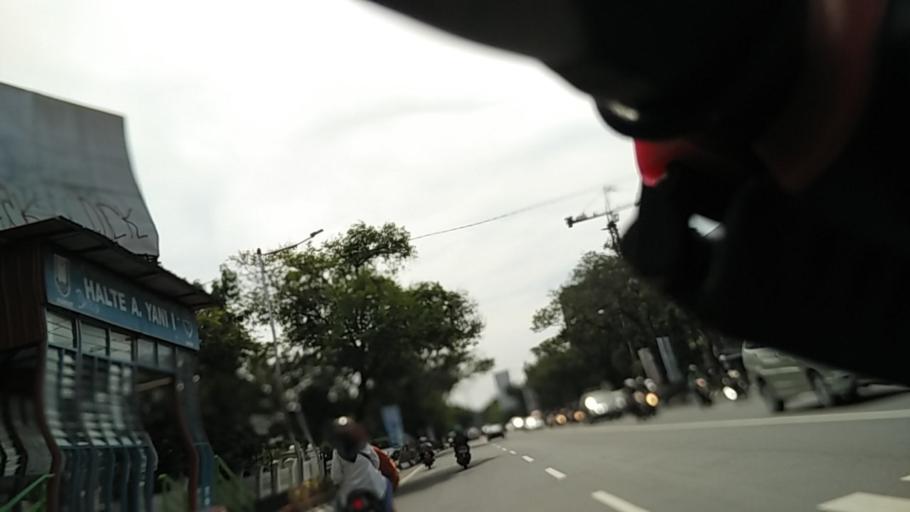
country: ID
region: Central Java
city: Semarang
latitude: -6.9922
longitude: 110.4272
